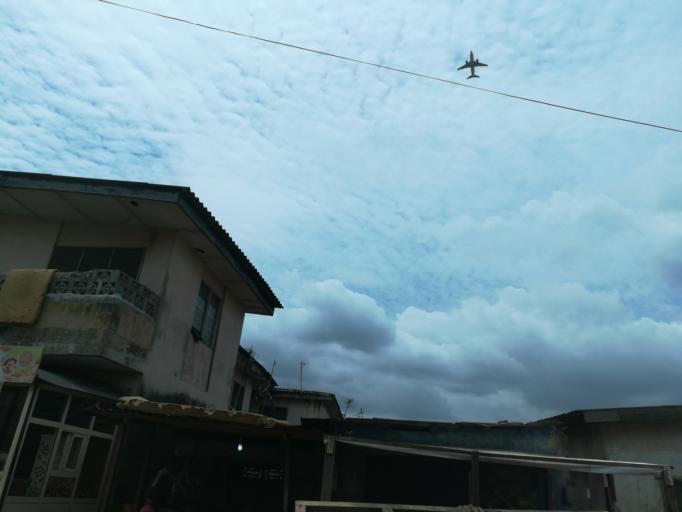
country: NG
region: Lagos
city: Oshodi
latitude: 6.5607
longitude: 3.3299
